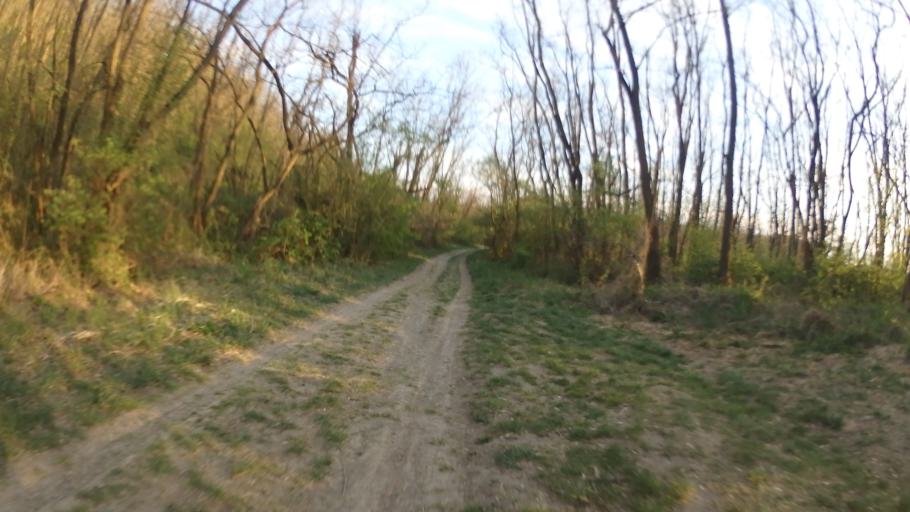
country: CZ
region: South Moravian
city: Moravany
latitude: 49.1320
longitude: 16.5569
